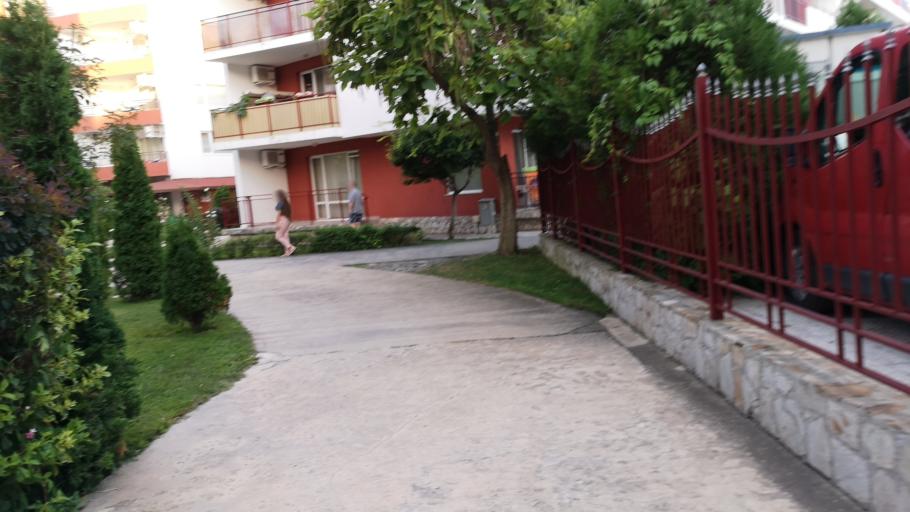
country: BG
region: Burgas
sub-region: Obshtina Nesebur
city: Sveti Vlas
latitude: 42.7030
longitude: 27.8072
